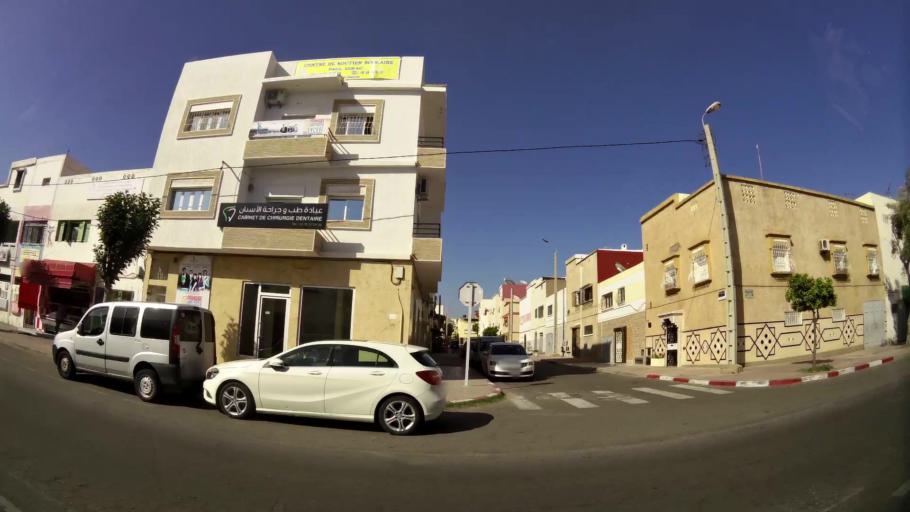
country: MA
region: Oued ed Dahab-Lagouira
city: Dakhla
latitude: 30.4231
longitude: -9.5622
